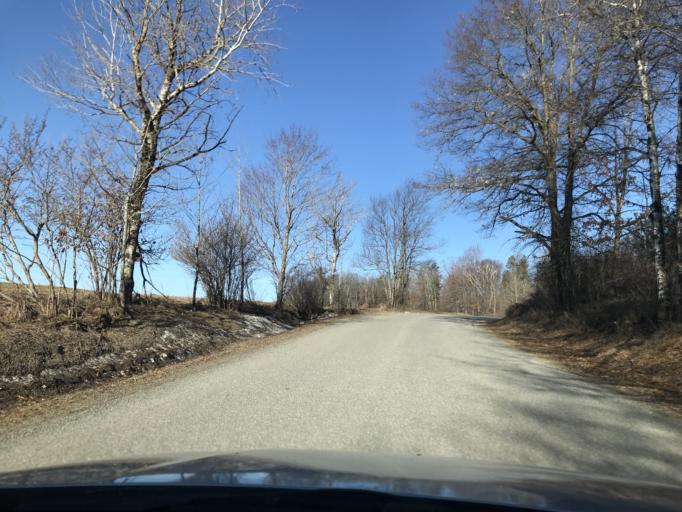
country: US
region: Wisconsin
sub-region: Marinette County
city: Niagara
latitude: 45.3807
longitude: -88.0377
